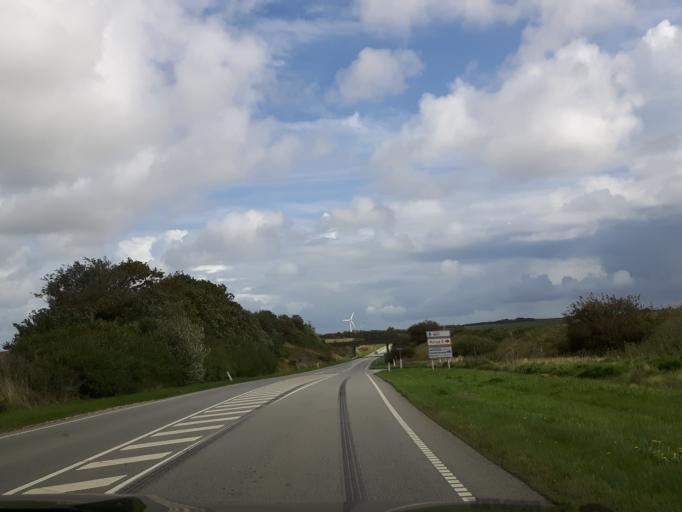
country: DK
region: North Denmark
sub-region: Thisted Kommune
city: Hurup
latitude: 56.7598
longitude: 8.4162
